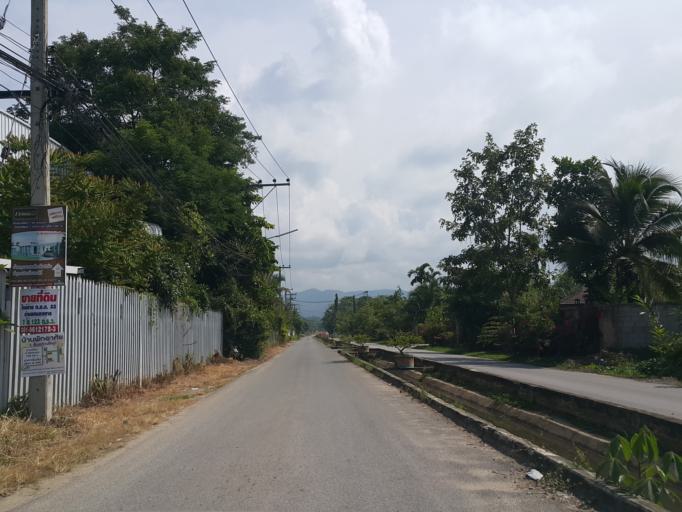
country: TH
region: Chiang Mai
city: San Sai
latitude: 18.9438
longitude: 98.9848
